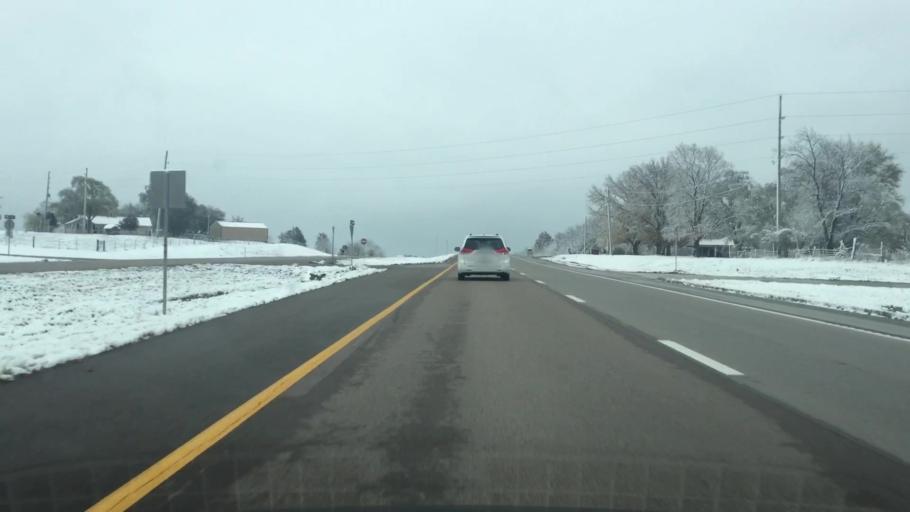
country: US
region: Missouri
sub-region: Cass County
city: Garden City
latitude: 38.4924
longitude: -94.0555
